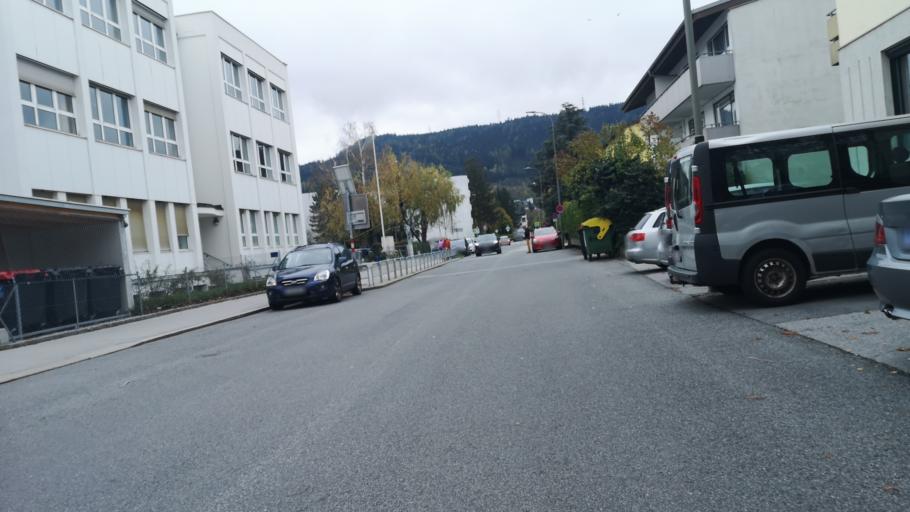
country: AT
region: Tyrol
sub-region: Innsbruck Stadt
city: Innsbruck
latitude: 47.2604
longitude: 11.3685
